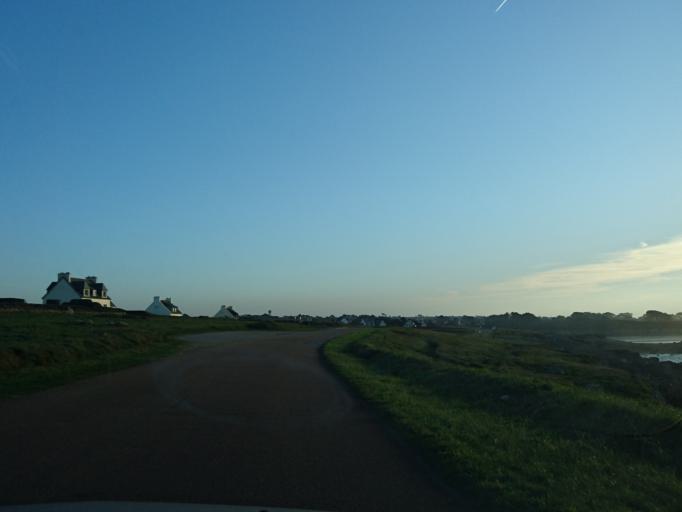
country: FR
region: Brittany
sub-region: Departement du Finistere
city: Landunvez
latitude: 48.5370
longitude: -4.7483
